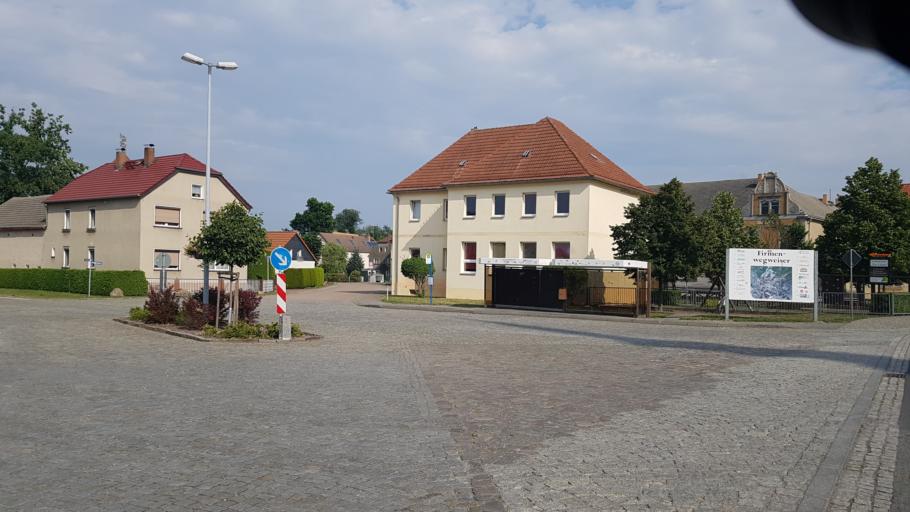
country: DE
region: Brandenburg
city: Grossthiemig
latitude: 51.3822
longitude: 13.6751
